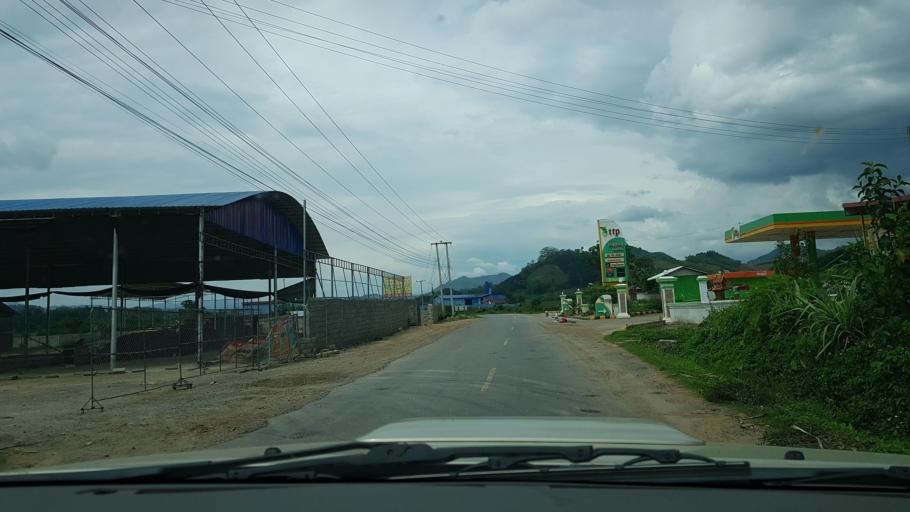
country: LA
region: Loungnamtha
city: Muang Nale
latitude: 20.3308
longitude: 101.6696
